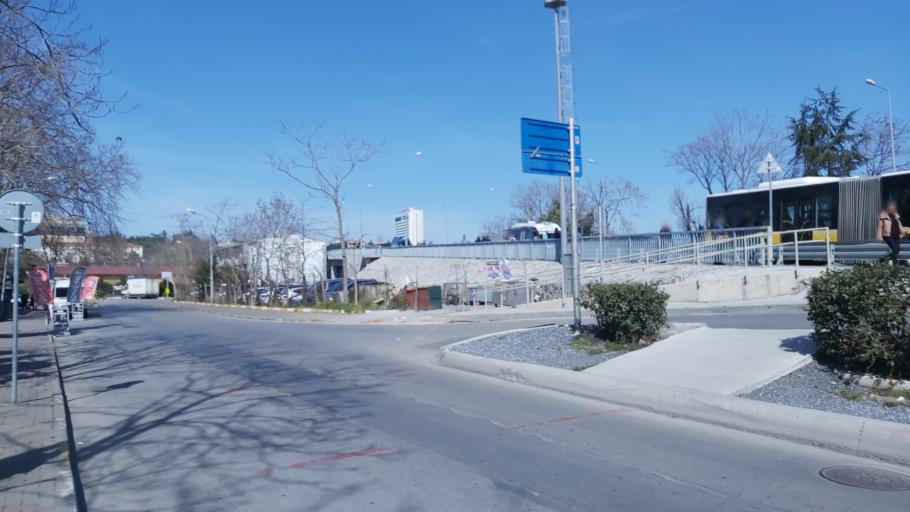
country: TR
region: Istanbul
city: UEskuedar
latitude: 40.9963
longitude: 29.0242
